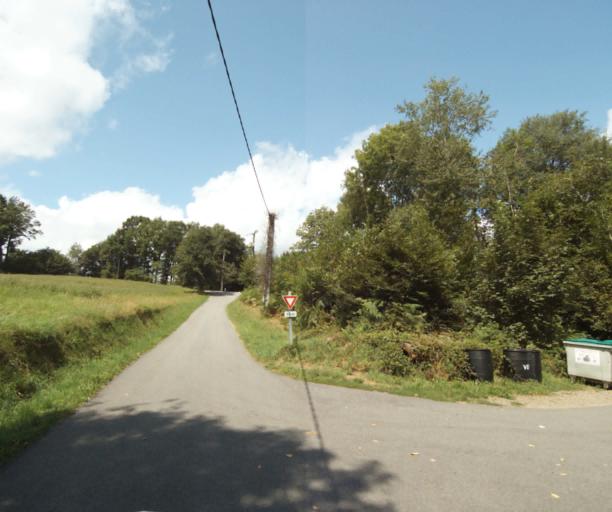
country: FR
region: Limousin
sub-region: Departement de la Correze
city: Sainte-Fortunade
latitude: 45.1977
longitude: 1.8232
